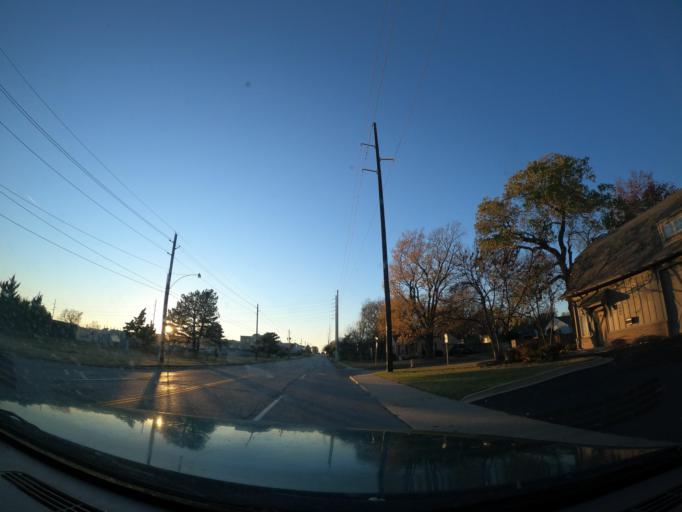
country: US
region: Oklahoma
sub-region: Tulsa County
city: Tulsa
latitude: 36.1407
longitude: -95.9166
